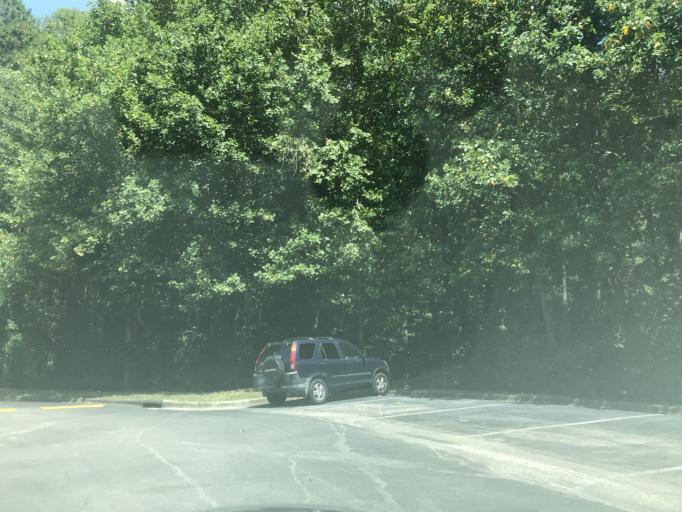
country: US
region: North Carolina
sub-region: Wake County
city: Raleigh
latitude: 35.8692
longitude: -78.5953
